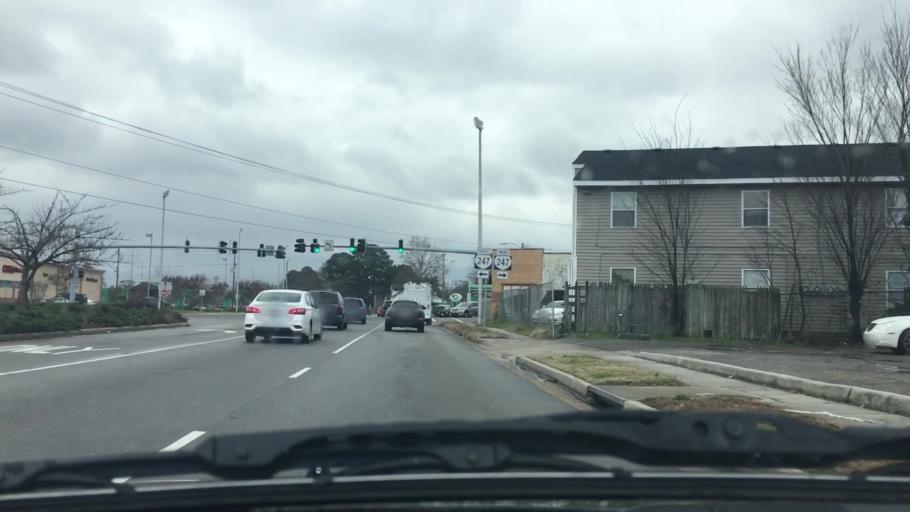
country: US
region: Virginia
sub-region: City of Norfolk
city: Norfolk
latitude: 36.8768
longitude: -76.2522
